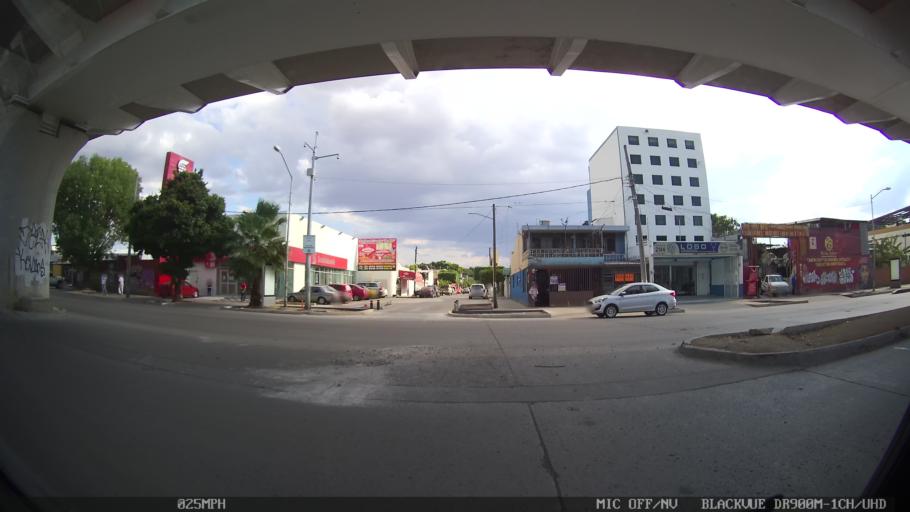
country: MX
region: Jalisco
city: Tlaquepaque
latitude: 20.6515
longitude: -103.3115
